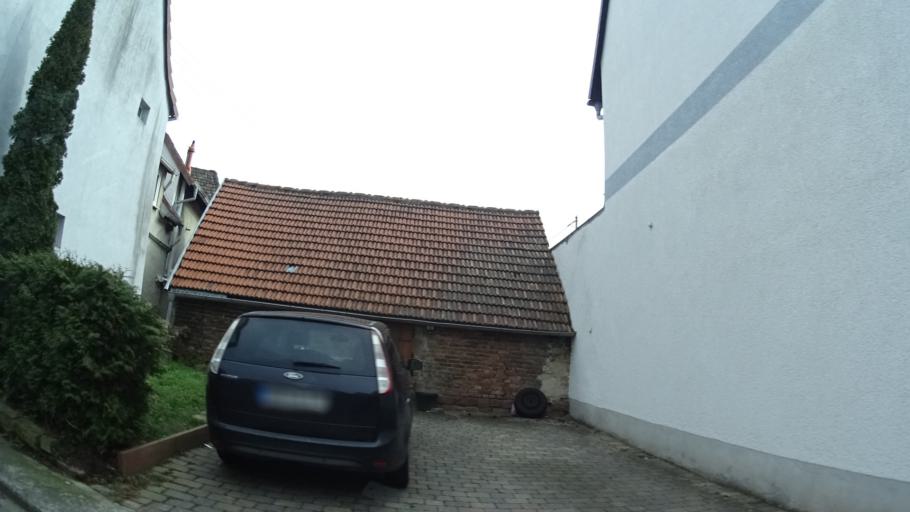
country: DE
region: Rheinland-Pfalz
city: Sankt Martin
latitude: 49.3013
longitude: 8.1026
